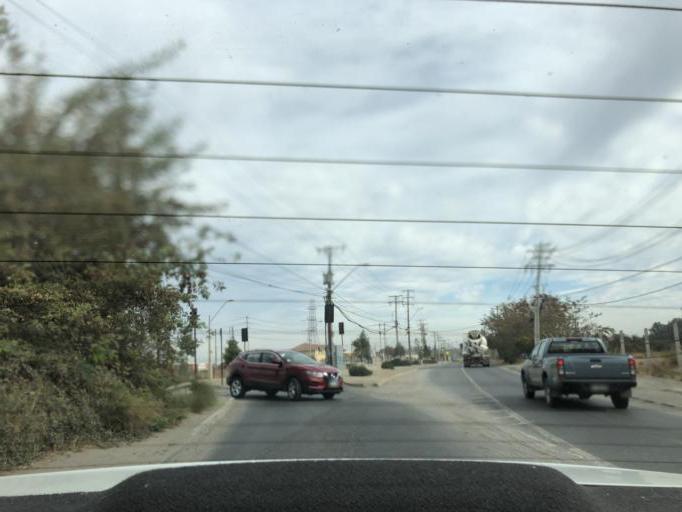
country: CL
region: Santiago Metropolitan
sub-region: Provincia de Cordillera
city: Puente Alto
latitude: -33.6114
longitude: -70.5430
